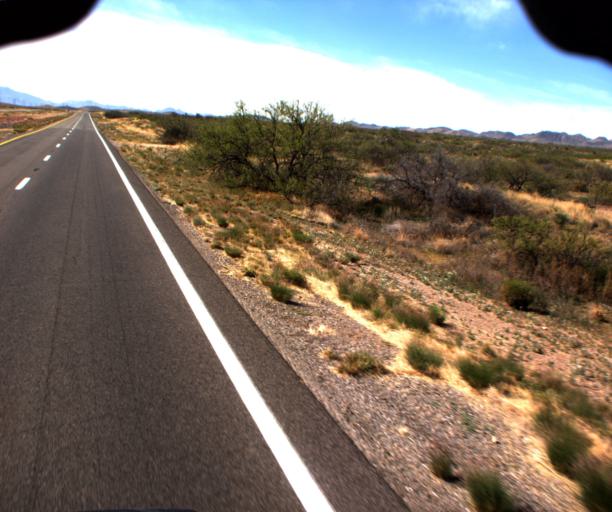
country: US
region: Arizona
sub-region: Graham County
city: Swift Trail Junction
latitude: 32.5046
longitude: -109.6743
